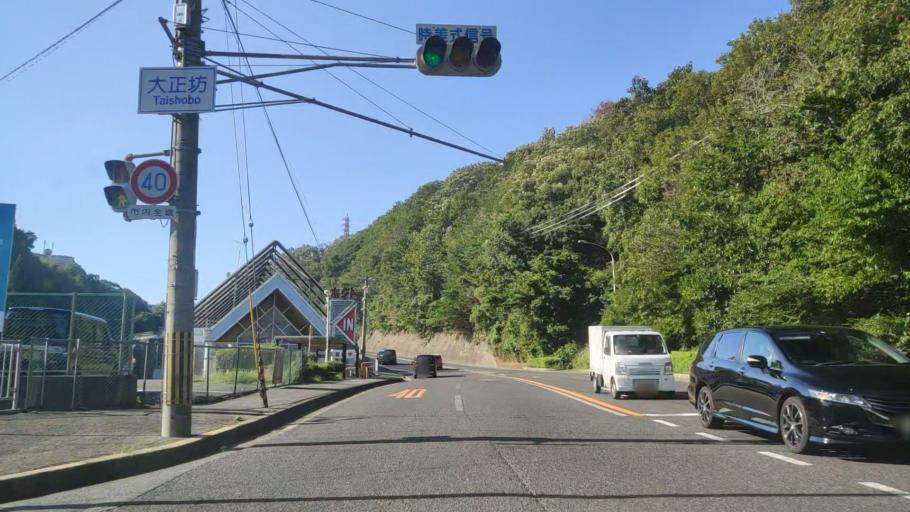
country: JP
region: Hyogo
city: Kobe
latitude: 34.7445
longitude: 135.1595
